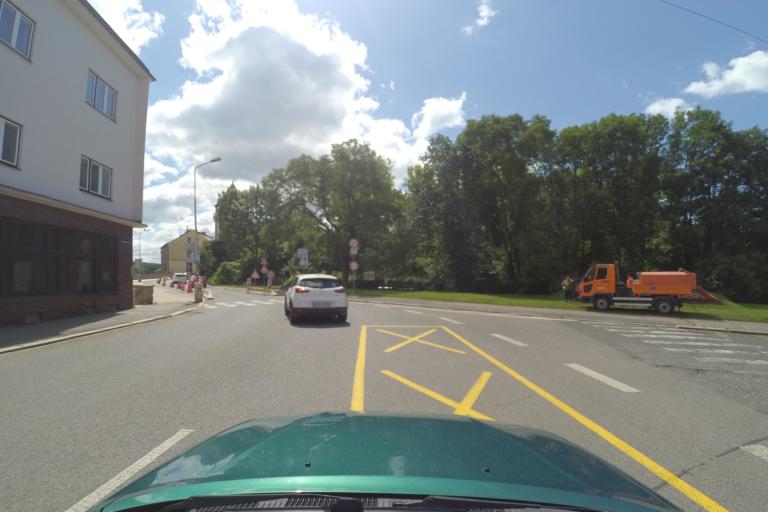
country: CZ
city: Nove Mesto nad Metuji
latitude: 50.3455
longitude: 16.1503
